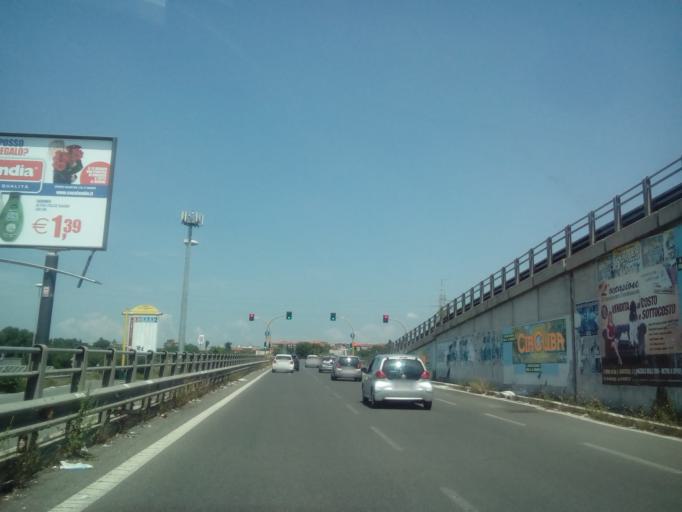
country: IT
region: Latium
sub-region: Citta metropolitana di Roma Capitale
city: Rome
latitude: 41.9197
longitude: 12.5654
